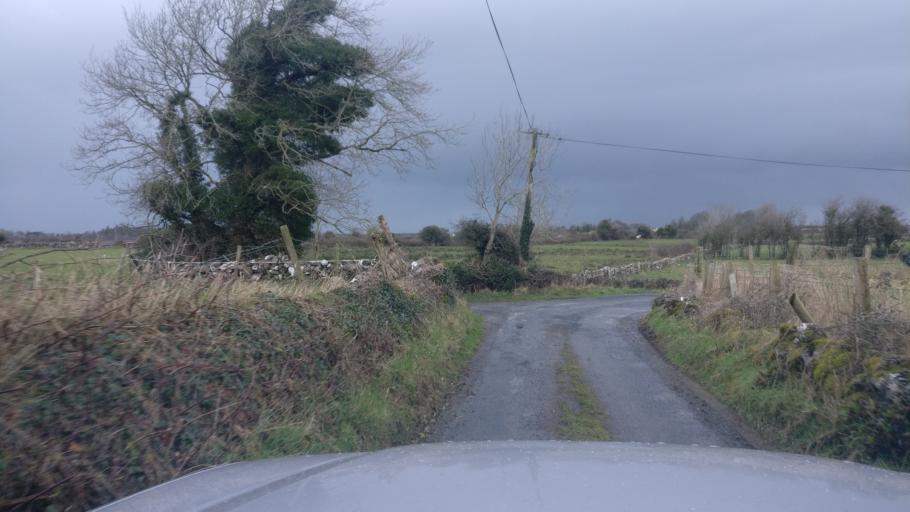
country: IE
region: Connaught
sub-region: County Galway
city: Loughrea
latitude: 53.2012
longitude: -8.6134
